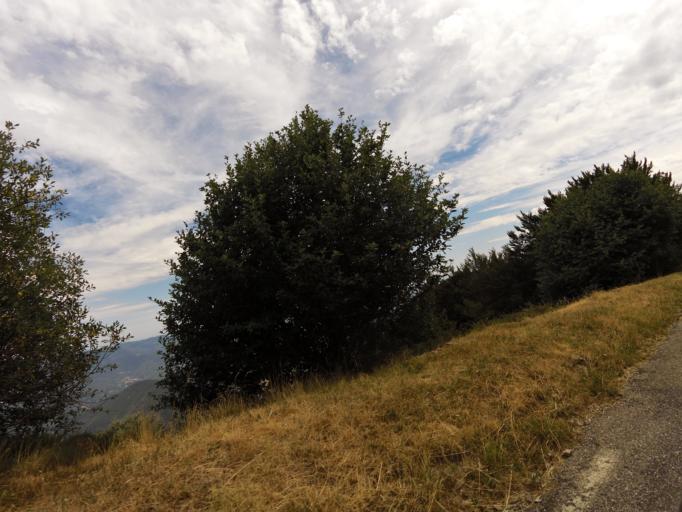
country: FR
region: Languedoc-Roussillon
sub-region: Departement du Gard
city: Valleraugue
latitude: 44.0581
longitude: 3.6060
